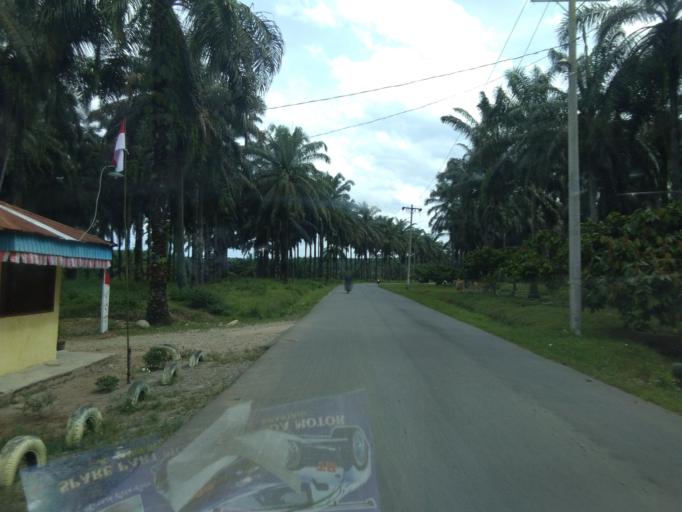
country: ID
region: North Sumatra
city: Deli Tua
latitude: 3.2958
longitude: 98.8074
